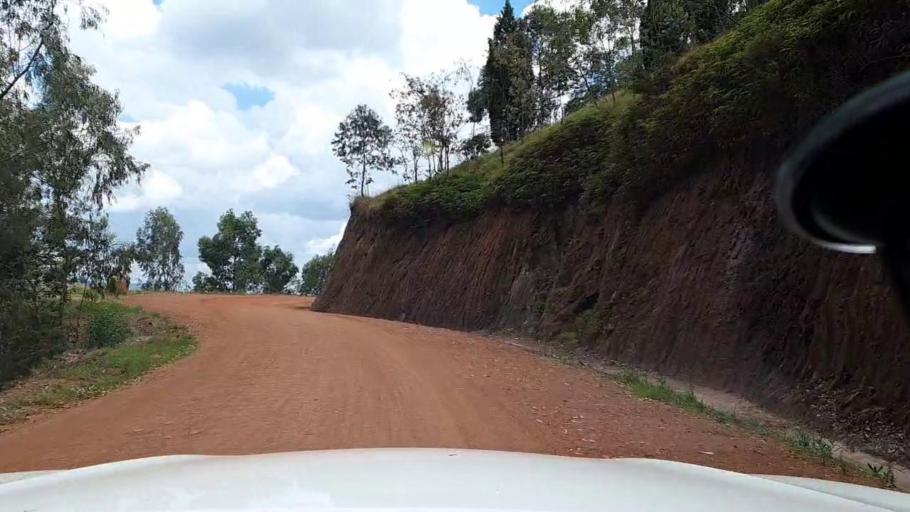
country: RW
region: Kigali
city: Kigali
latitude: -1.7851
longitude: 29.8447
